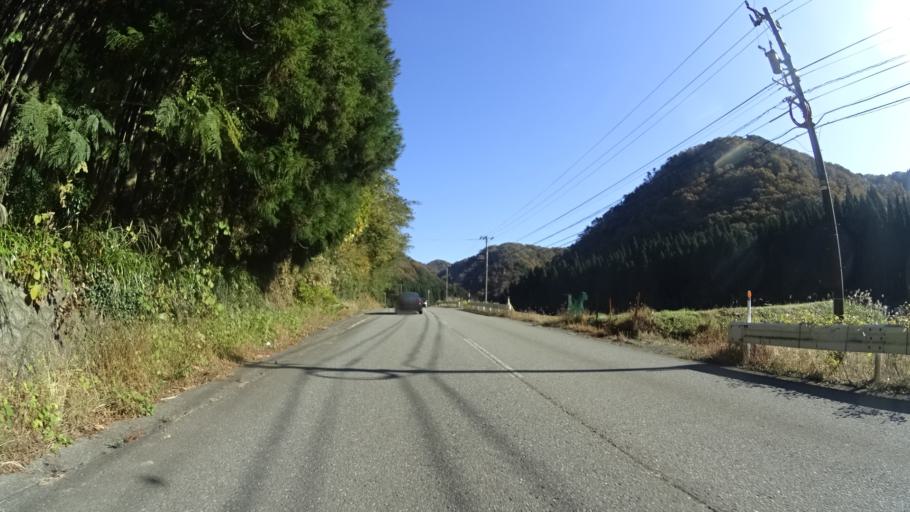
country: JP
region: Ishikawa
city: Tsurugi-asahimachi
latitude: 36.3718
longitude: 136.5611
